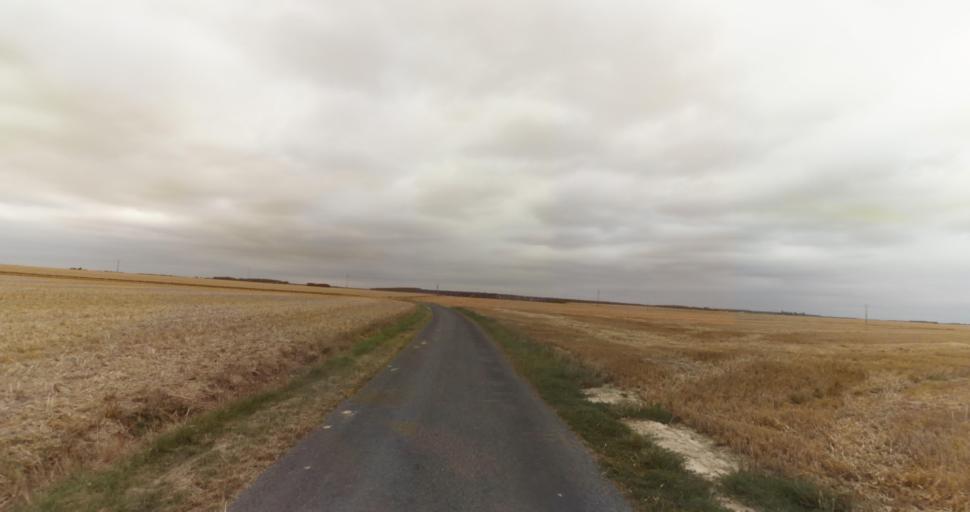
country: FR
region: Haute-Normandie
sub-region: Departement de l'Eure
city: La Couture-Boussey
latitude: 48.9357
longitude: 1.3315
